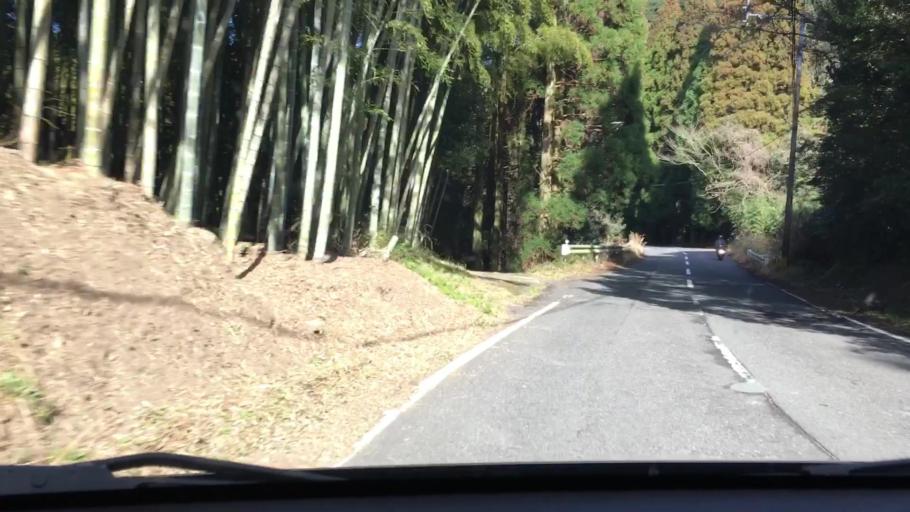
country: JP
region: Kagoshima
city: Ijuin
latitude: 31.7288
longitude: 130.4189
